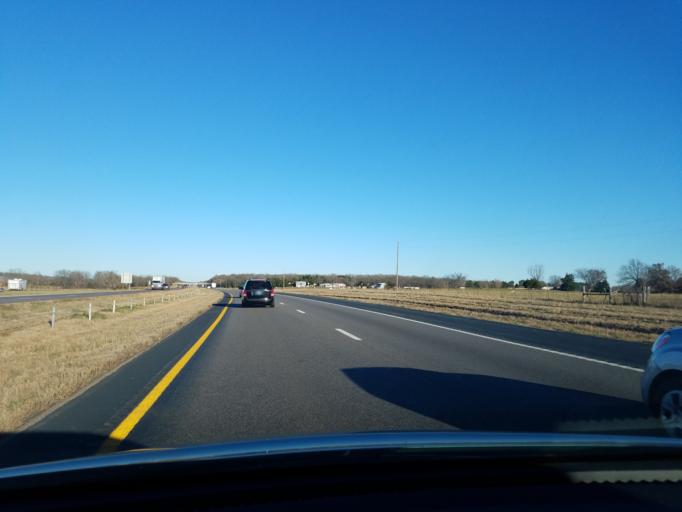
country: US
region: Missouri
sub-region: Crawford County
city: Cuba
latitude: 38.0466
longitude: -91.4677
